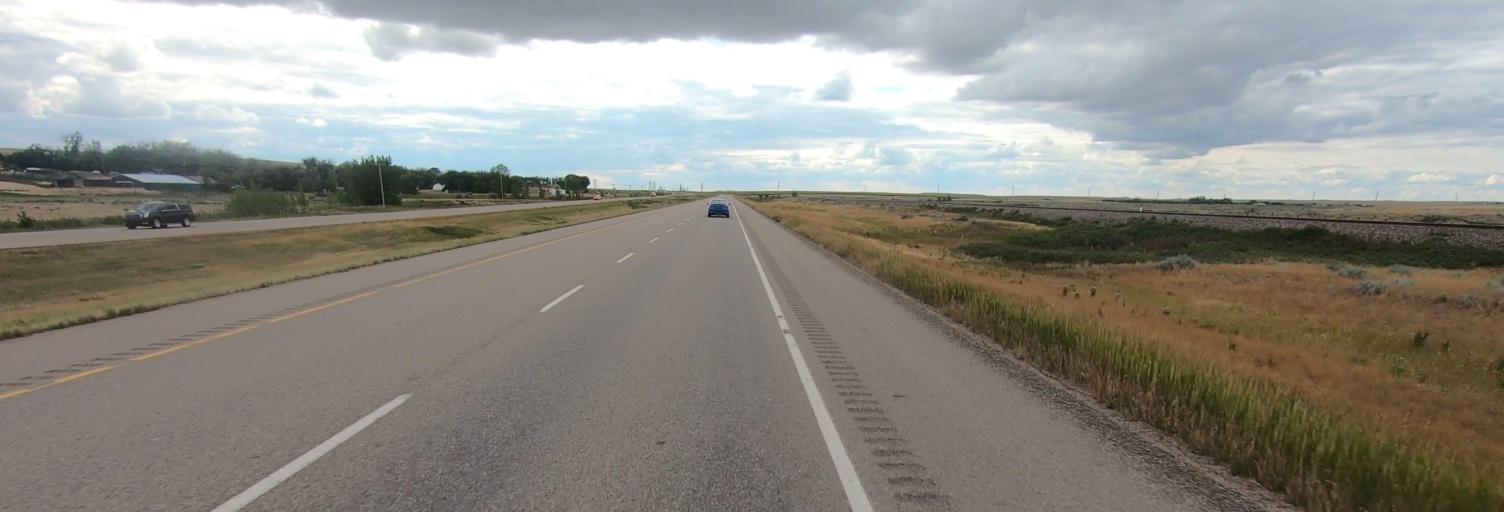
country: CA
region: Alberta
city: Medicine Hat
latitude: 49.9833
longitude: -110.4307
